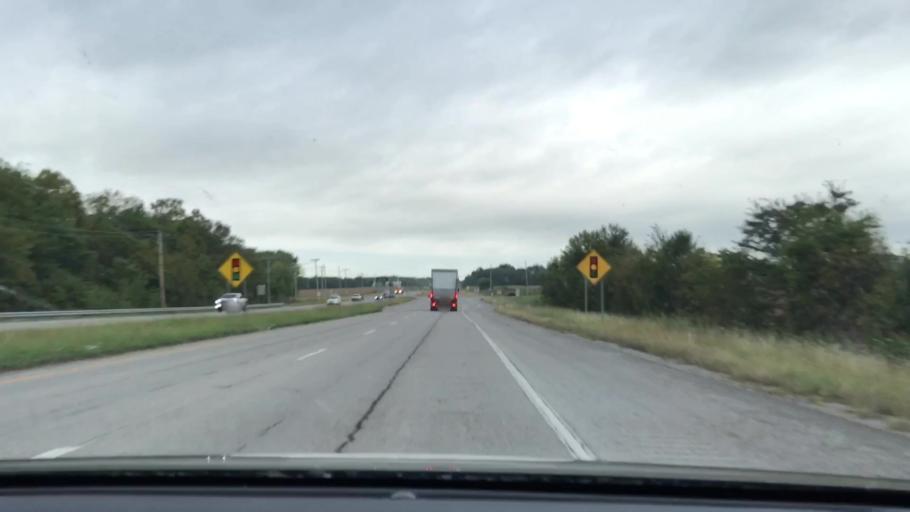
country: US
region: Kentucky
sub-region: Christian County
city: Hopkinsville
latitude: 36.8331
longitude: -87.5265
